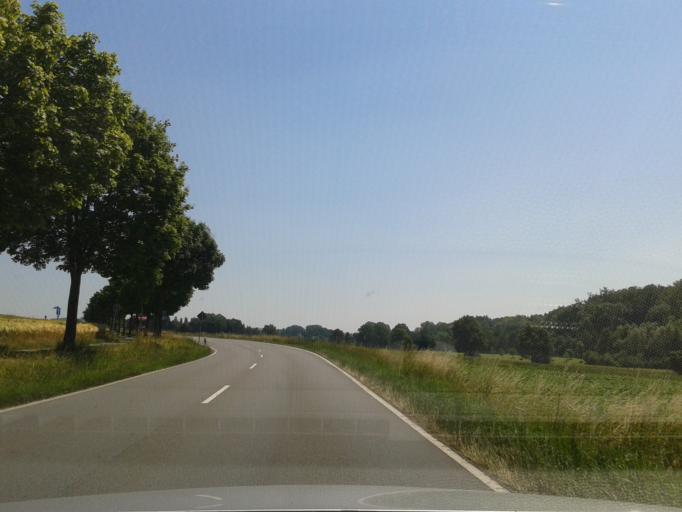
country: DE
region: North Rhine-Westphalia
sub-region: Regierungsbezirk Detmold
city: Dorentrup
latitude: 52.0317
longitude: 9.0129
